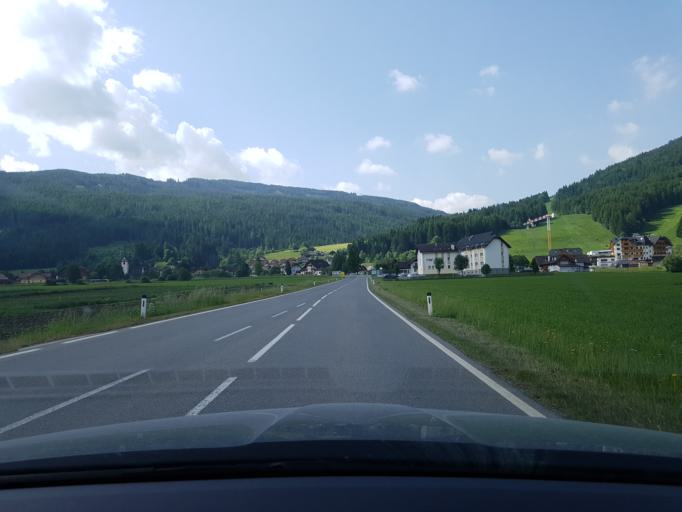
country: AT
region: Salzburg
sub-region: Politischer Bezirk Tamsweg
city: Sankt Margarethen im Lungau
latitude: 47.0844
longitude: 13.6925
